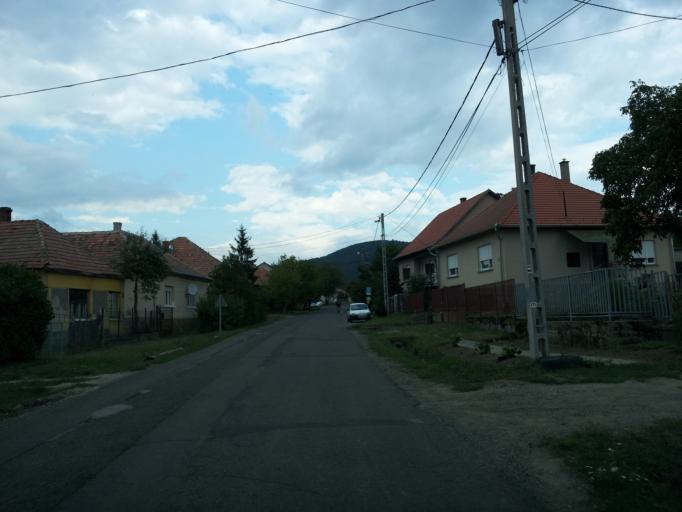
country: HU
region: Pest
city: Szob
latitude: 47.8723
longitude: 18.9299
